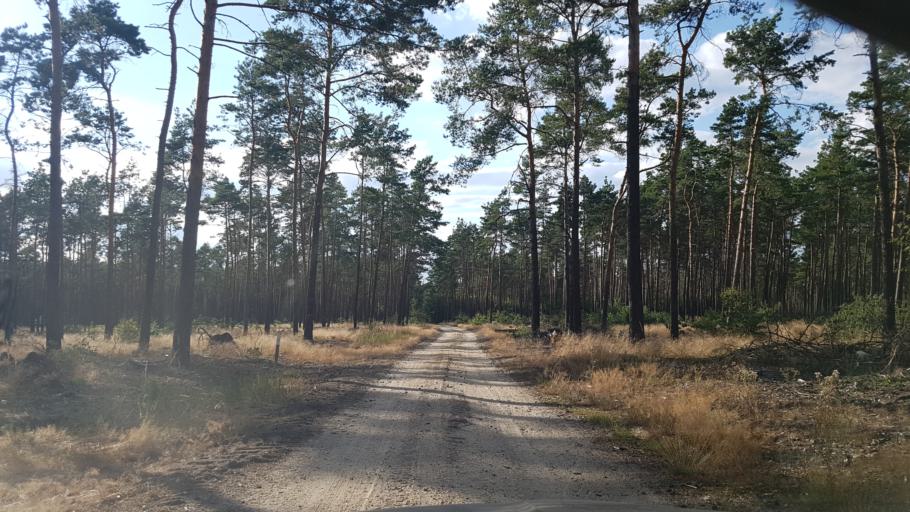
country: DE
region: Brandenburg
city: Trobitz
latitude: 51.6230
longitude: 13.4145
